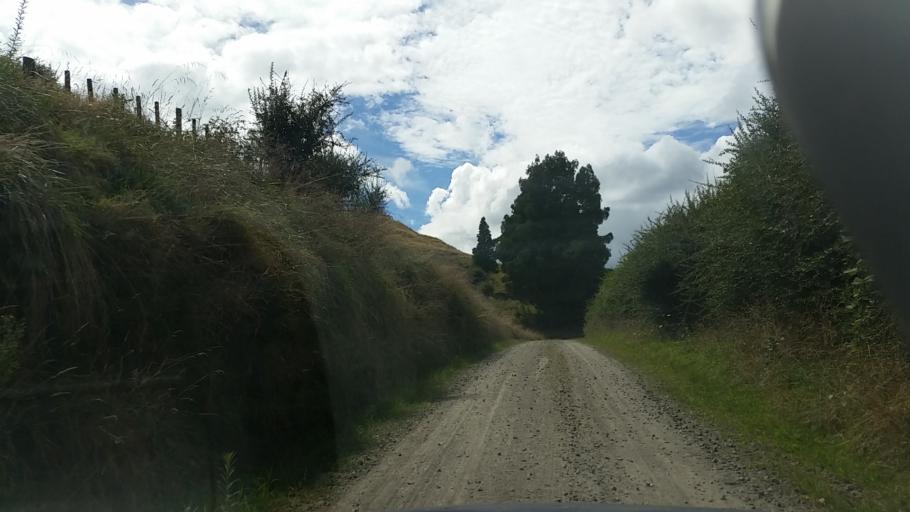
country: NZ
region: Taranaki
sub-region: South Taranaki District
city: Eltham
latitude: -39.2573
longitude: 174.5675
